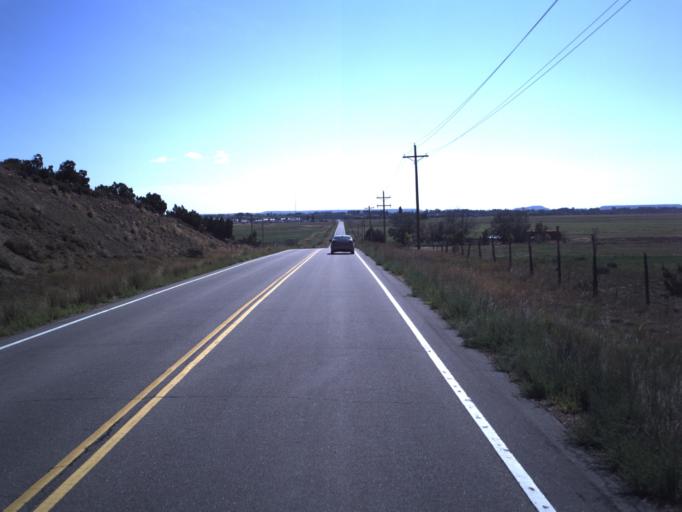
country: US
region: Utah
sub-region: Duchesne County
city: Duchesne
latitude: 40.3556
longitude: -110.3507
